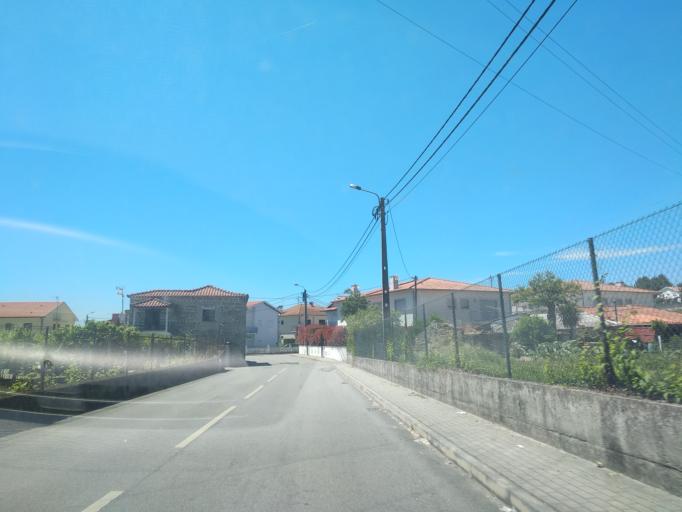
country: PT
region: Braga
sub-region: Braga
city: Braga
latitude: 41.5247
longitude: -8.4591
